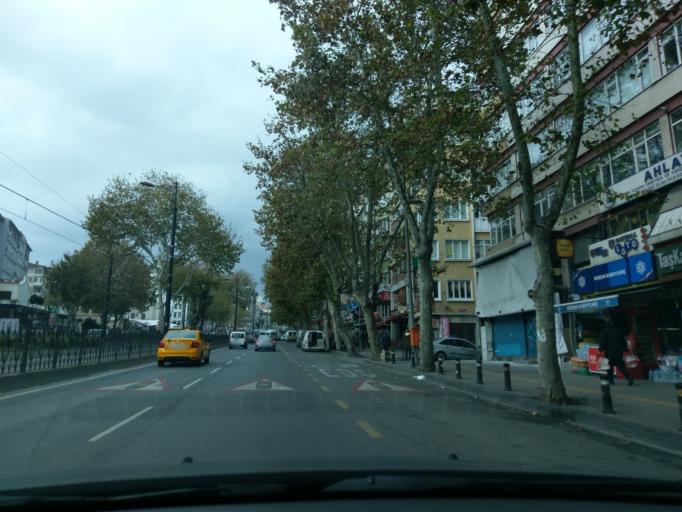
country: TR
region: Istanbul
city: Istanbul
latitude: 41.0112
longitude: 28.9429
